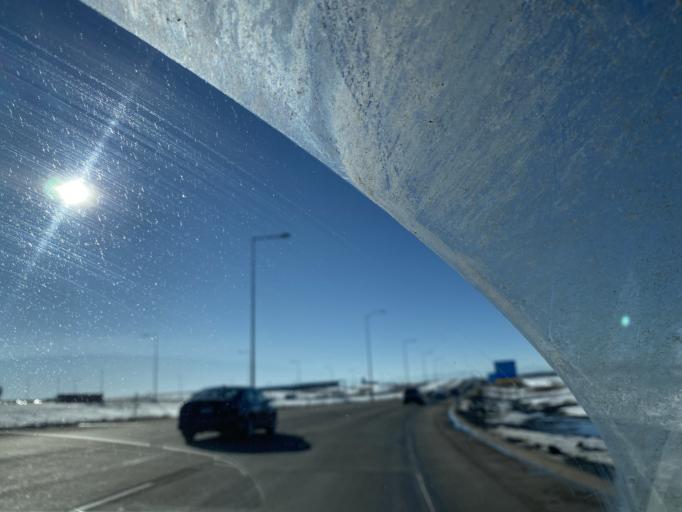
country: US
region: Colorado
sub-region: Weld County
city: Lochbuie
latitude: 39.8353
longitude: -104.6790
